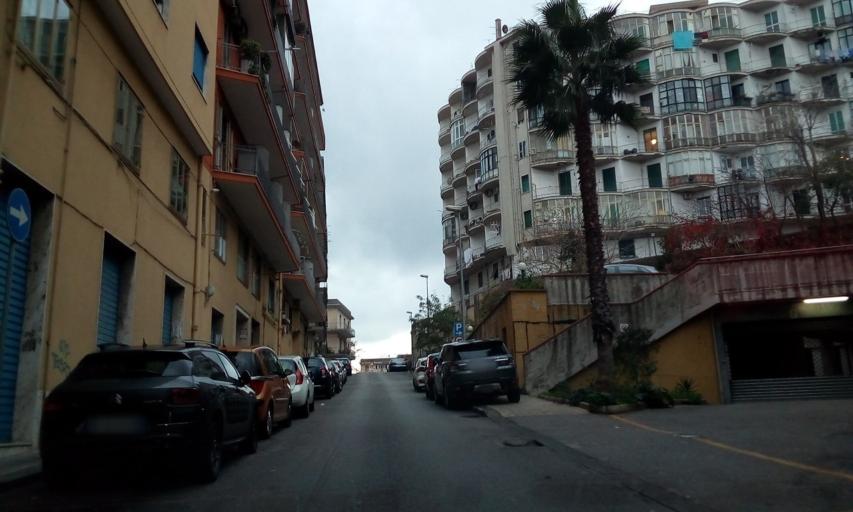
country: IT
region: Campania
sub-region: Provincia di Salerno
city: Capezzano Inferiore
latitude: 40.6864
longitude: 14.7700
